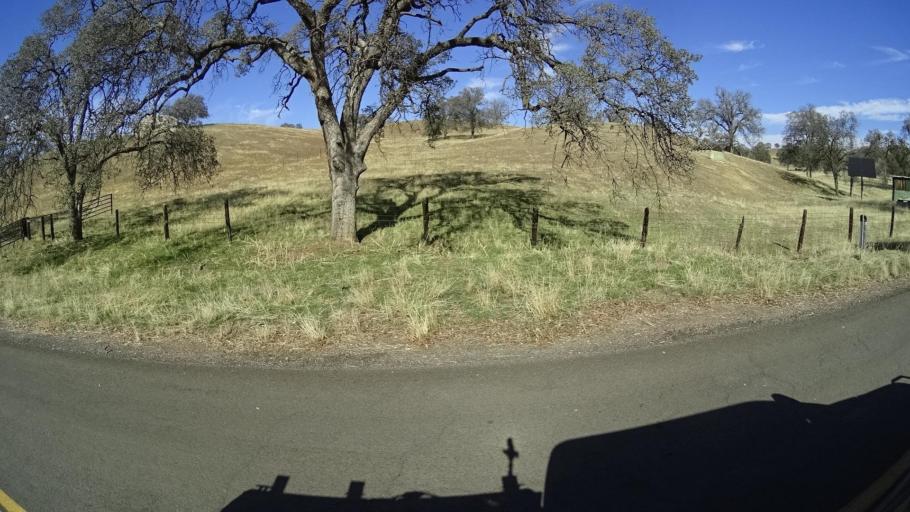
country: US
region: California
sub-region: Tulare County
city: Richgrove
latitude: 35.6754
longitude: -118.8519
